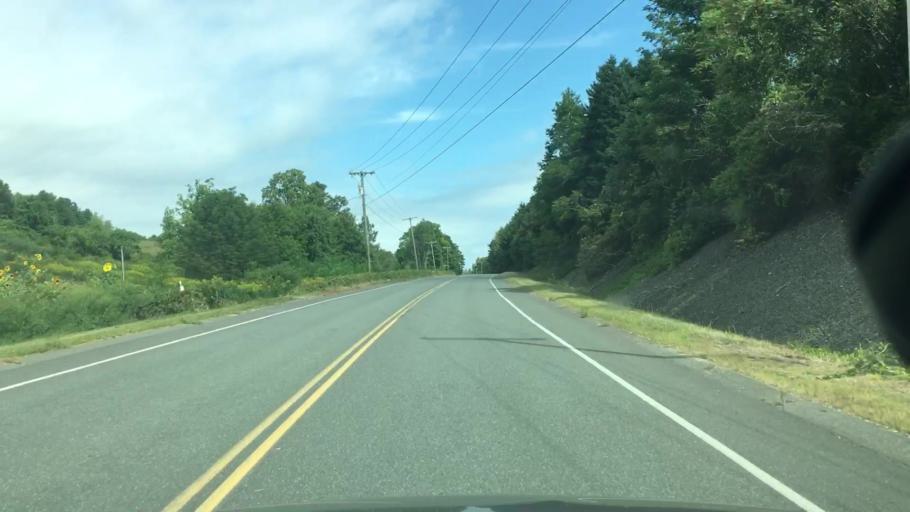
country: US
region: Massachusetts
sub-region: Franklin County
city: Colrain
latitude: 42.6439
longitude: -72.6746
